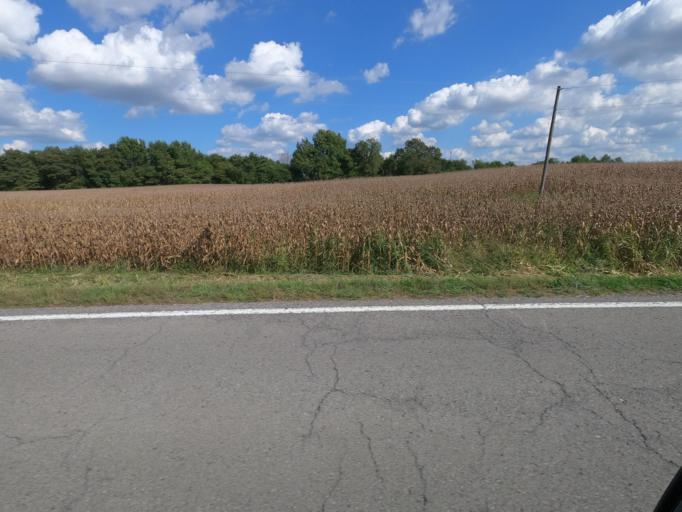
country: US
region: Illinois
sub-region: Massac County
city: Metropolis
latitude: 37.2768
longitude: -88.7548
